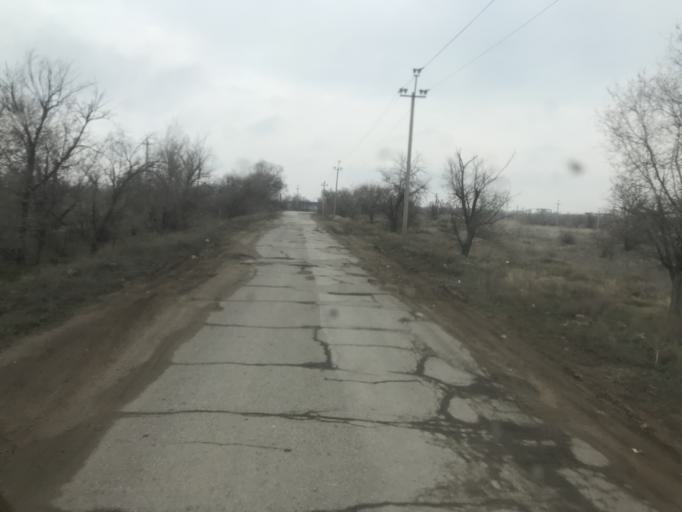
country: RU
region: Volgograd
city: Krasnoslobodsk
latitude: 48.5326
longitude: 44.6070
